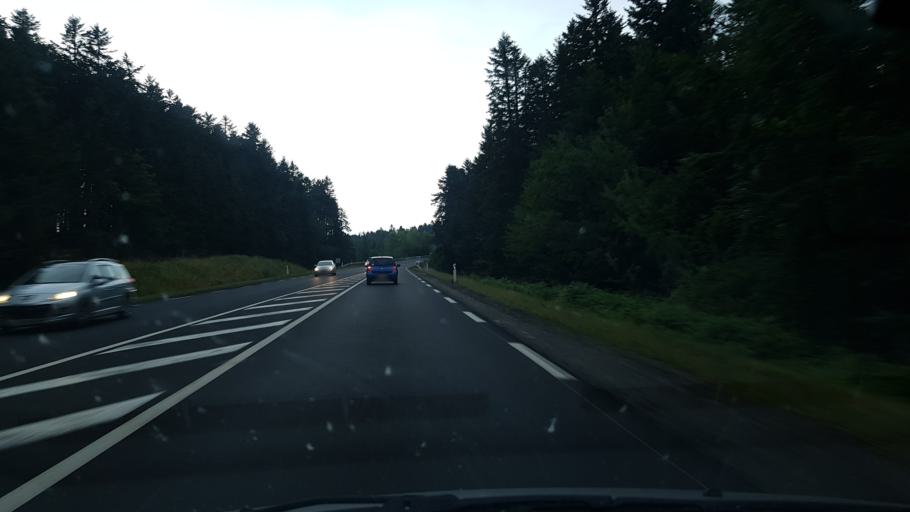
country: FR
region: Auvergne
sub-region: Departement de la Haute-Loire
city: Allegre
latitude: 45.1431
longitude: 3.6451
